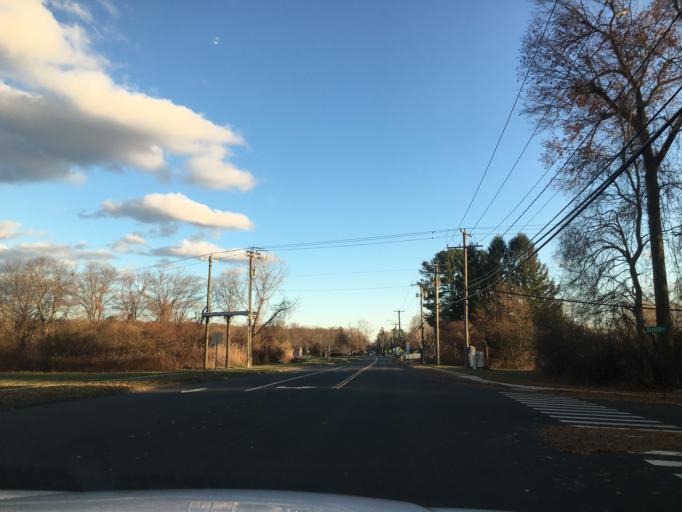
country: US
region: Connecticut
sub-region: Hartford County
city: Southwood Acres
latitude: 41.9634
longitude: -72.5794
